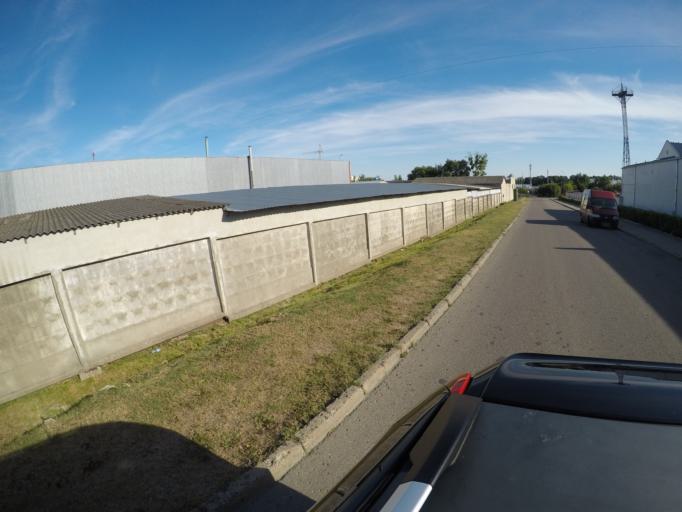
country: BY
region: Grodnenskaya
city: Hrodna
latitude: 53.7115
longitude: 23.8363
